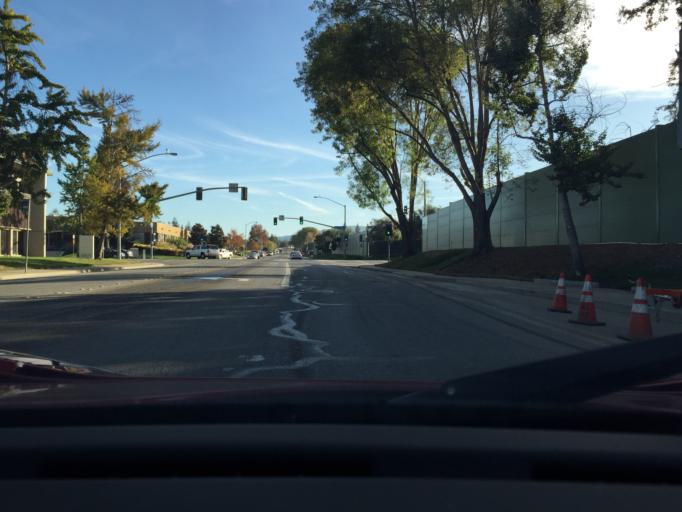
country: US
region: California
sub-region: Santa Clara County
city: Cupertino
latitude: 37.3330
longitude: -122.0059
